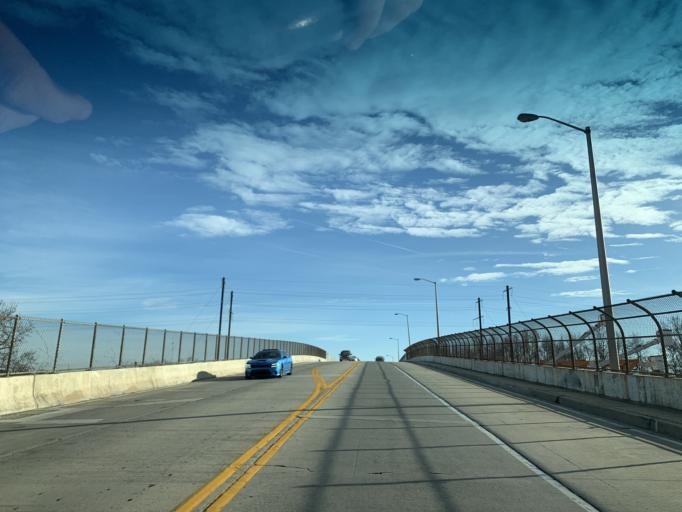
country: US
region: Maryland
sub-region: Cecil County
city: Elkton
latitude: 39.6119
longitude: -75.8365
